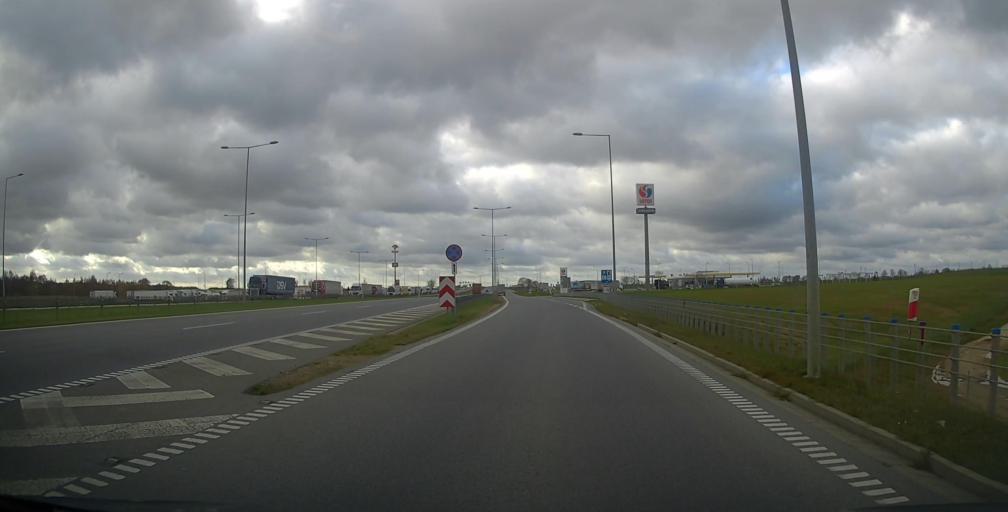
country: PL
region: Podlasie
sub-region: Powiat suwalski
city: Raczki
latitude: 53.9998
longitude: 22.8290
